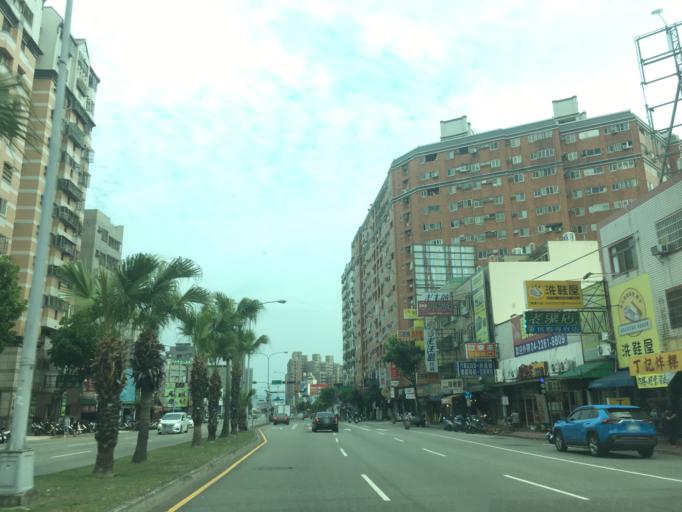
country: TW
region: Taiwan
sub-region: Taichung City
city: Taichung
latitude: 24.1146
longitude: 120.6558
